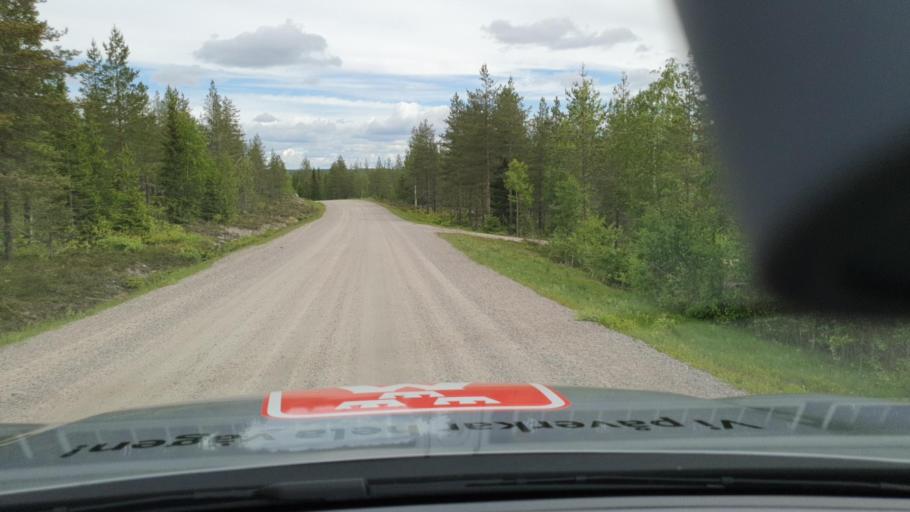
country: SE
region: Norrbotten
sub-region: Kalix Kommun
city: Kalix
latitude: 65.9305
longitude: 23.5250
